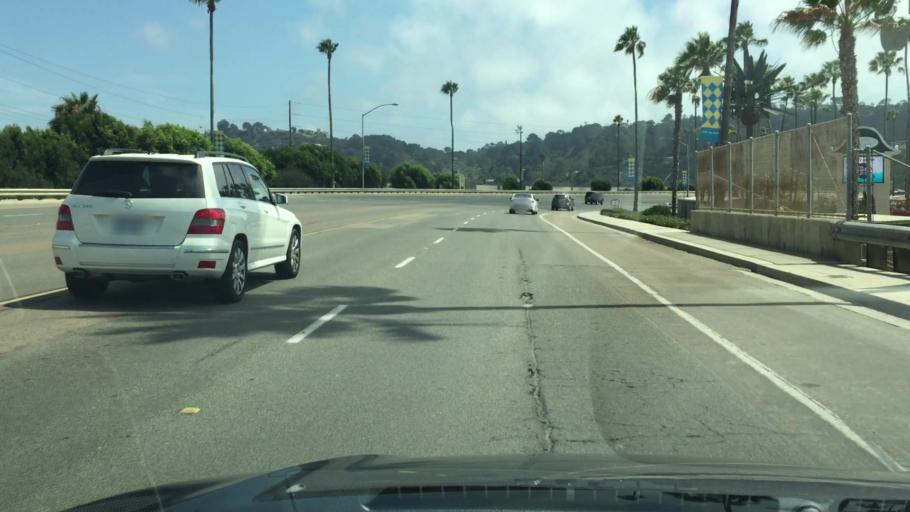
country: US
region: California
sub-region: San Diego County
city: Del Mar
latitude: 32.9747
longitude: -117.2563
